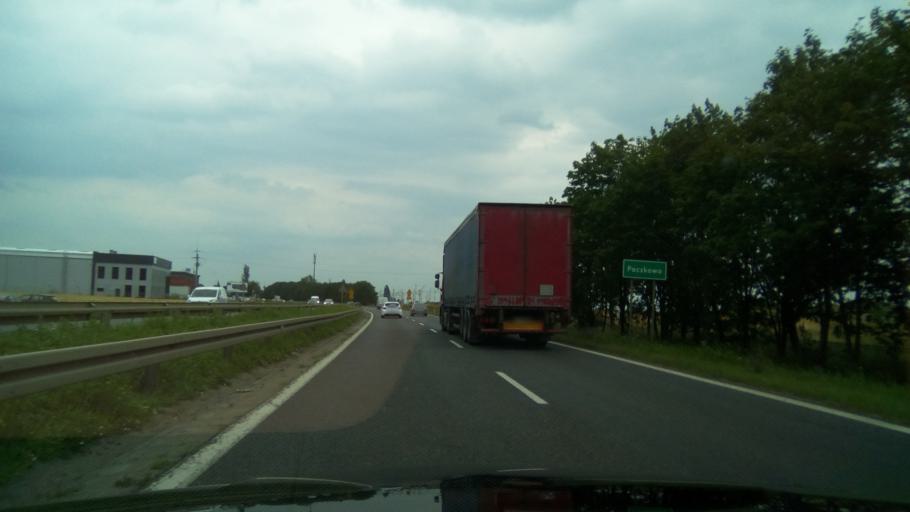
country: PL
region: Greater Poland Voivodeship
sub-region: Powiat poznanski
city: Swarzedz
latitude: 52.3991
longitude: 17.1404
